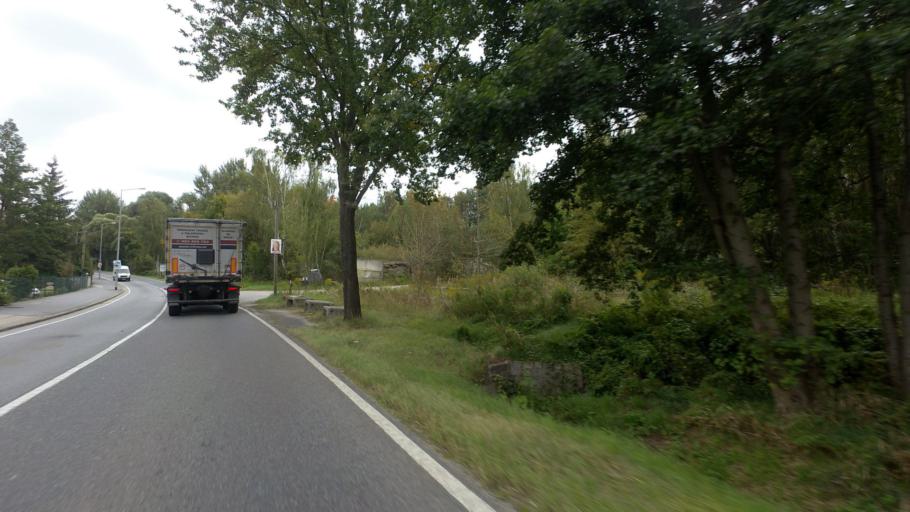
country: DE
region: Saxony
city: Bautzen
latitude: 51.1939
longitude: 14.4099
